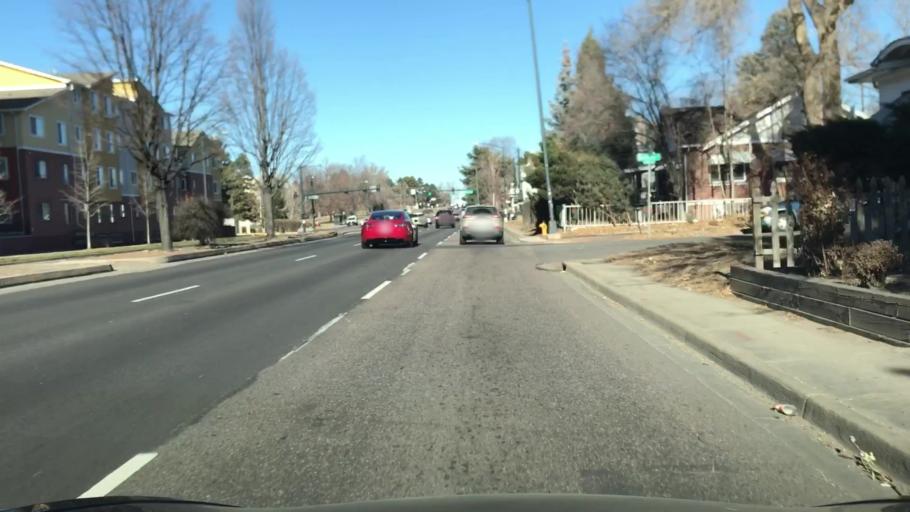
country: US
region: Colorado
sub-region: Arapahoe County
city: Glendale
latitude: 39.7423
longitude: -104.9406
